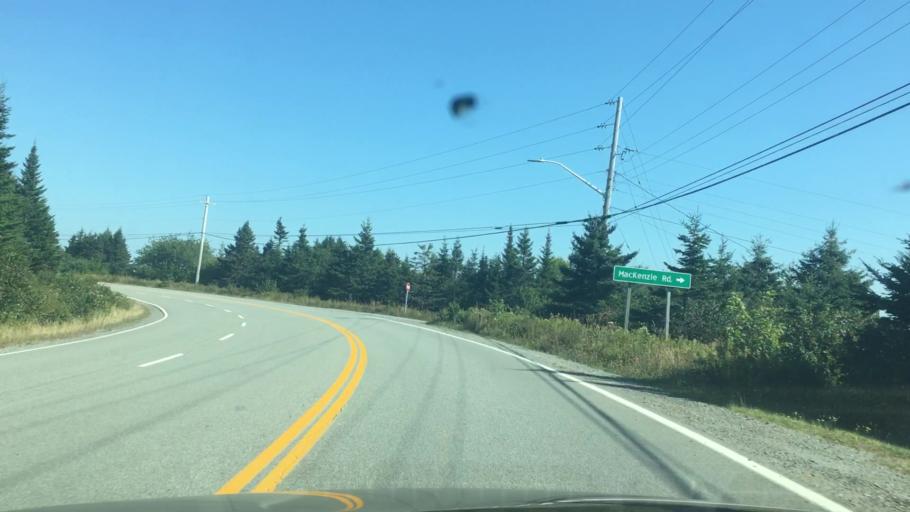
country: CA
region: Nova Scotia
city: New Glasgow
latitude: 44.8146
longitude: -62.6315
